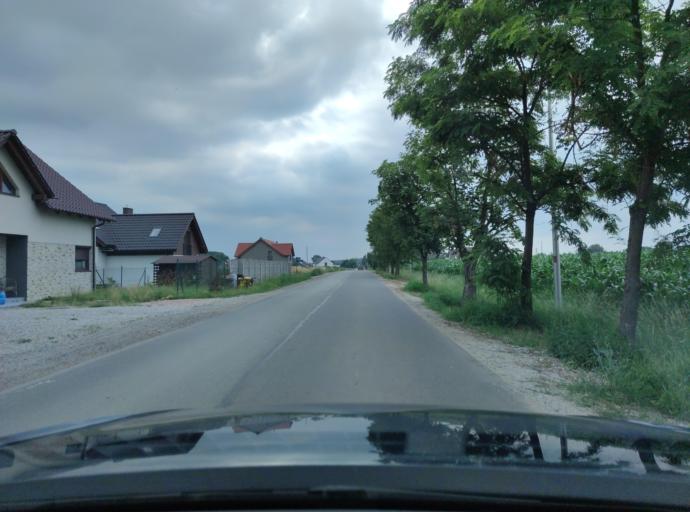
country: PL
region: Lower Silesian Voivodeship
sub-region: Powiat wroclawski
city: Tyniec Maly
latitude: 50.9985
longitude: 16.9120
